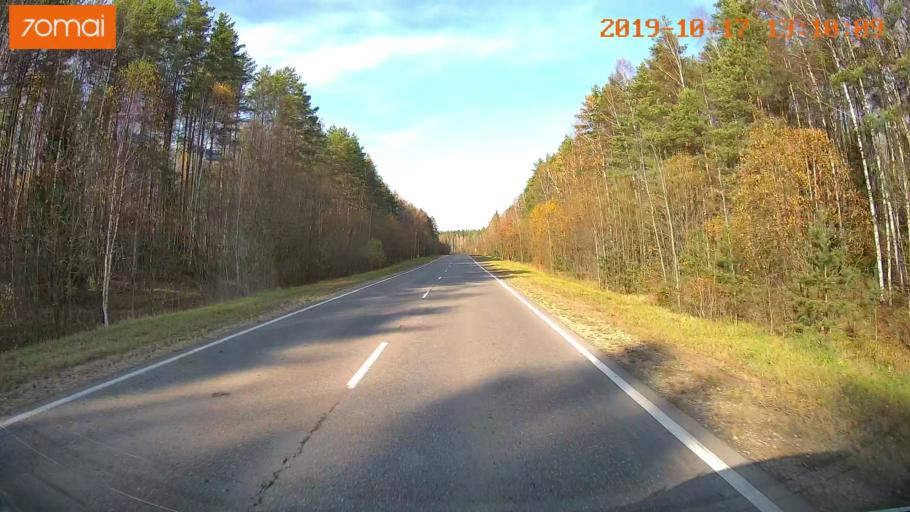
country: RU
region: Rjazan
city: Syntul
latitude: 55.0145
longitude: 41.2584
